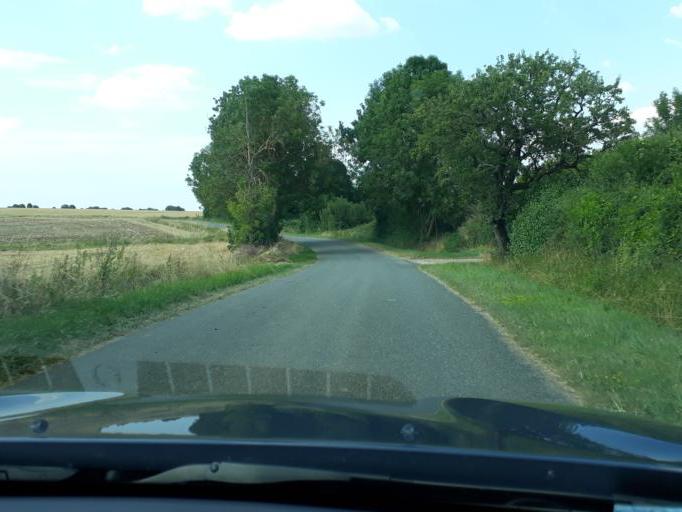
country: FR
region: Centre
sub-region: Departement du Cher
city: Nerondes
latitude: 47.0329
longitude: 2.8981
